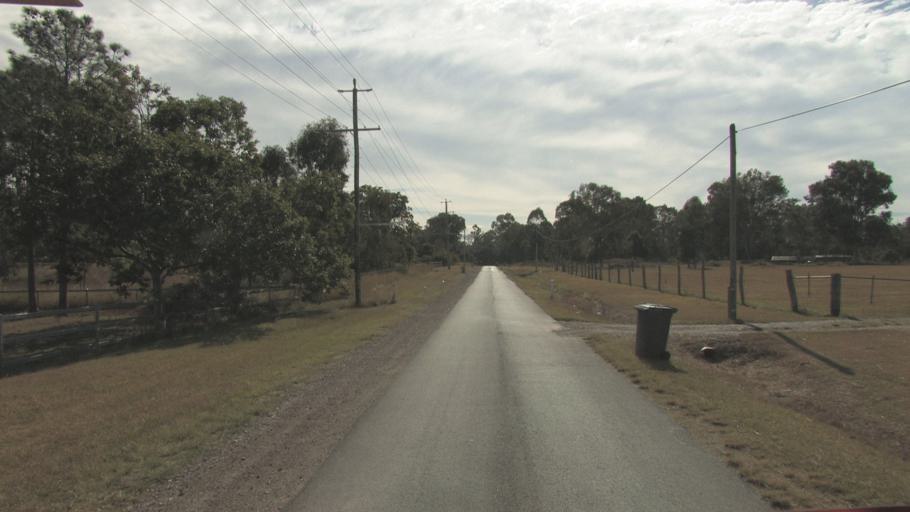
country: AU
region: Queensland
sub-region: Logan
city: North Maclean
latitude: -27.7777
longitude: 153.0081
